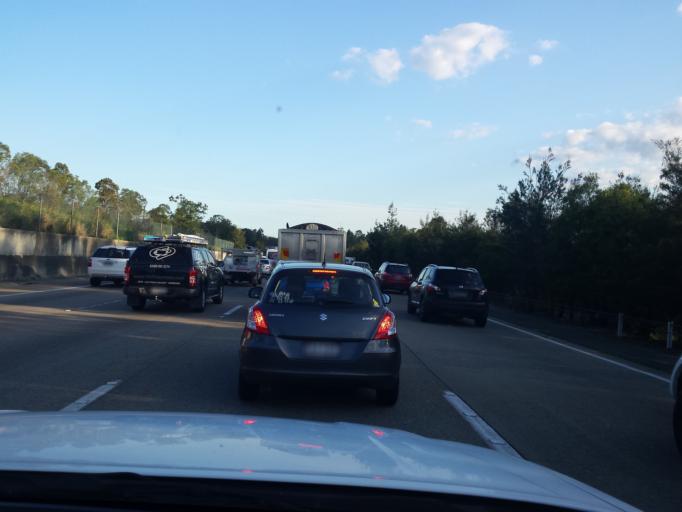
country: AU
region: Queensland
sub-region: Gold Coast
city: Oxenford
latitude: -27.8423
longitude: 153.3043
